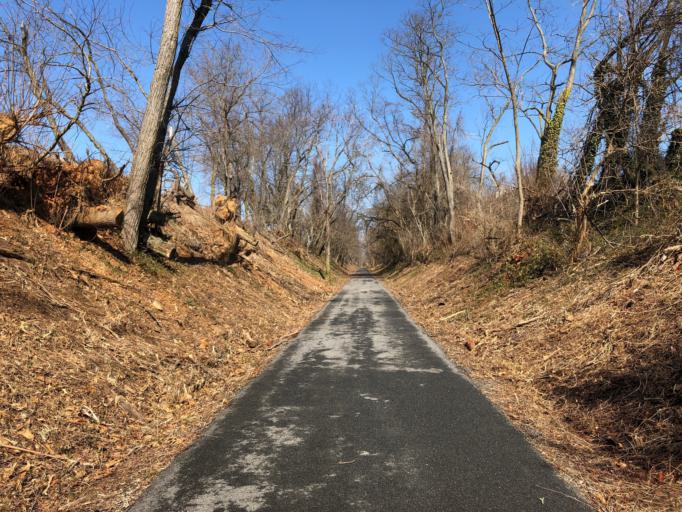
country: US
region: Maryland
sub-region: Kent County
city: Chestertown
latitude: 39.2185
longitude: -76.0716
